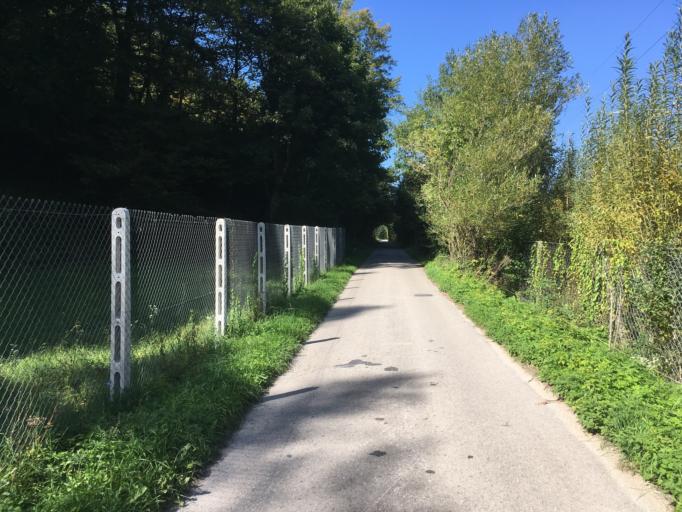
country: SK
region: Trenciansky
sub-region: Okres Povazska Bystrica
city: Povazska Bystrica
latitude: 49.0303
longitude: 18.4347
